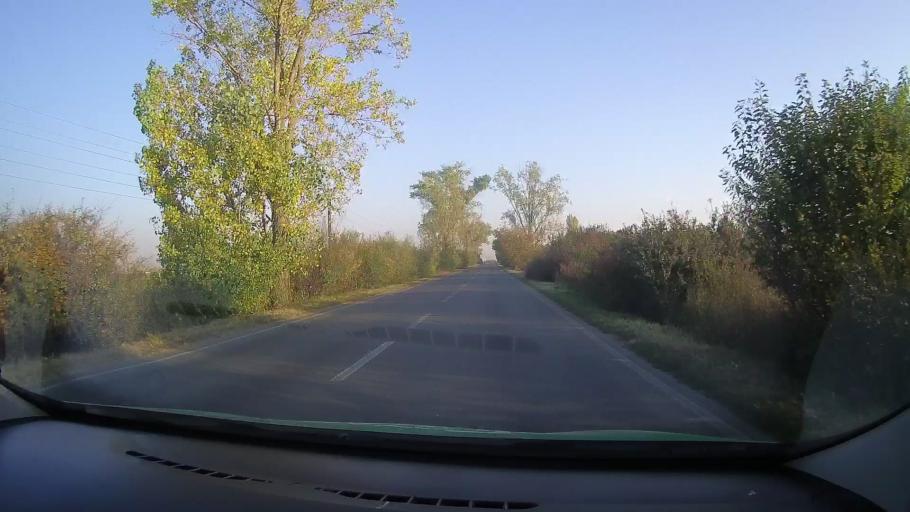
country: RO
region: Arad
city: Arad
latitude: 46.2240
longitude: 21.3205
